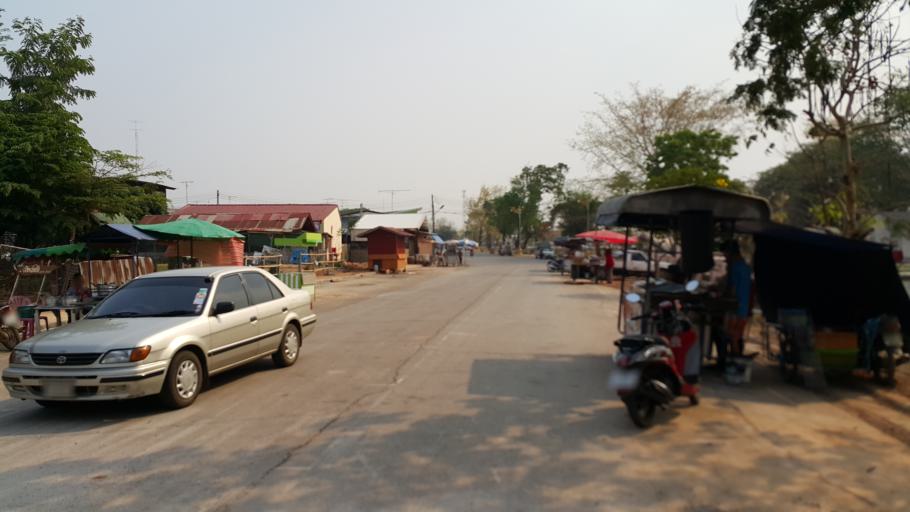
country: TH
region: Nakhon Phanom
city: That Phanom
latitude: 16.9450
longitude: 104.7274
